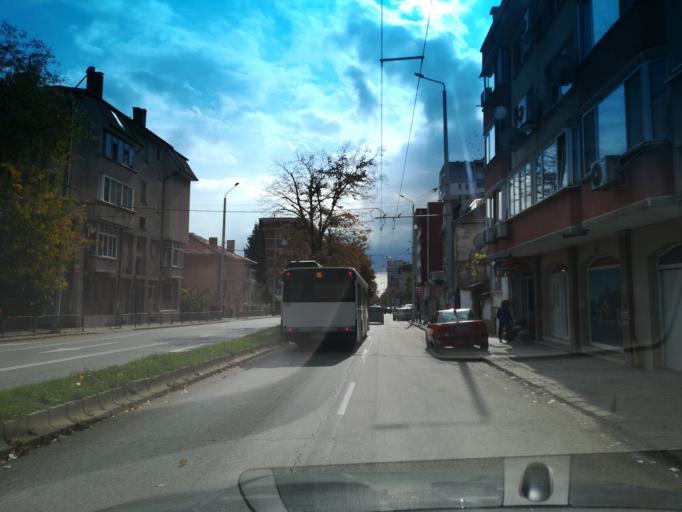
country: BG
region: Stara Zagora
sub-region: Obshtina Stara Zagora
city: Stara Zagora
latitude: 42.4330
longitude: 25.6323
